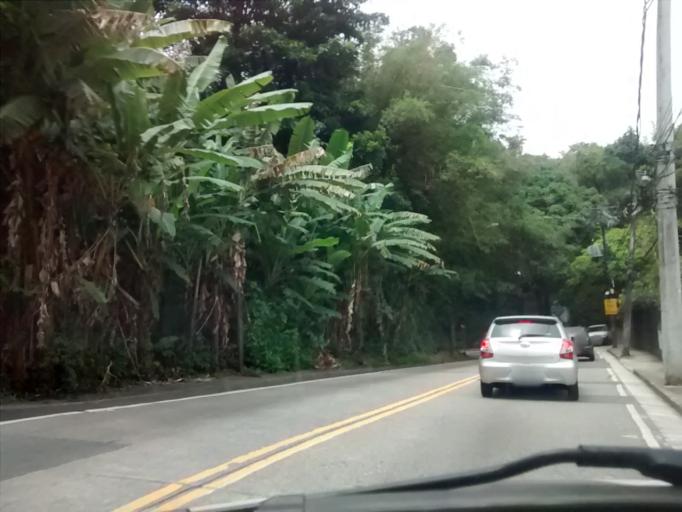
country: BR
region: Rio de Janeiro
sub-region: Rio De Janeiro
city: Rio de Janeiro
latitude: -22.9673
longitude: -43.2785
